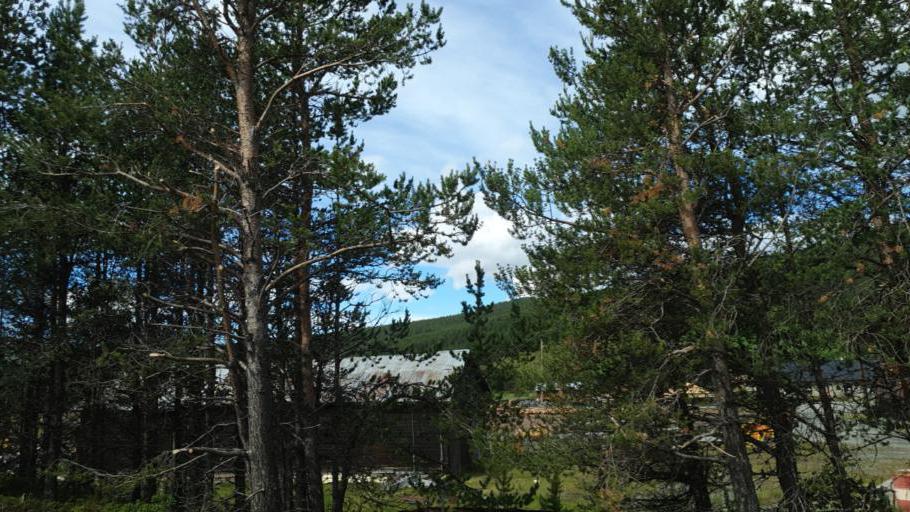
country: NO
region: Oppland
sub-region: Vaga
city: Vagamo
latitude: 61.7210
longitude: 9.0586
